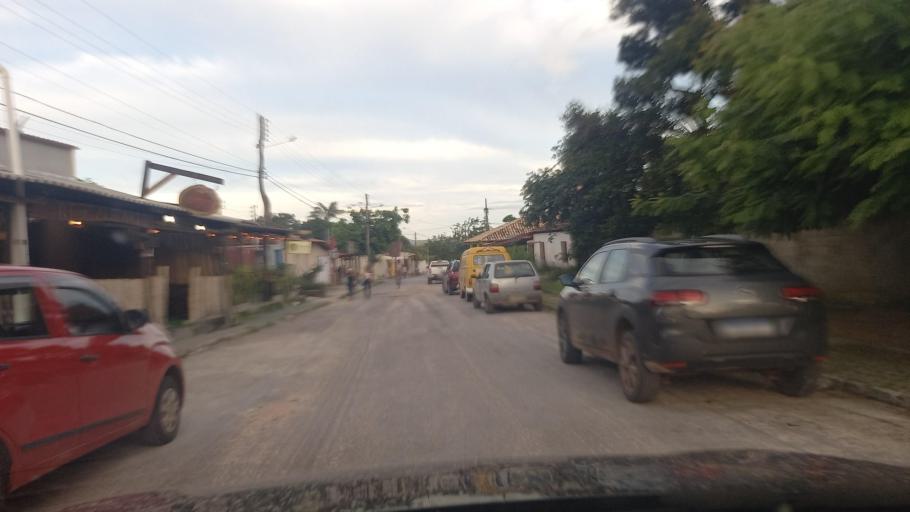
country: BR
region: Goias
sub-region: Cavalcante
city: Cavalcante
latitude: -13.7981
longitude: -47.4600
